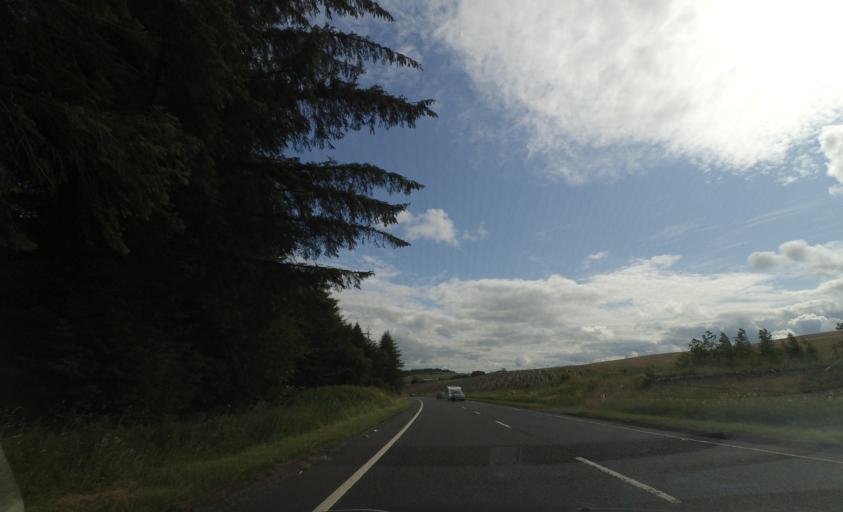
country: GB
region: Scotland
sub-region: The Scottish Borders
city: Selkirk
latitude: 55.5194
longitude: -2.8352
